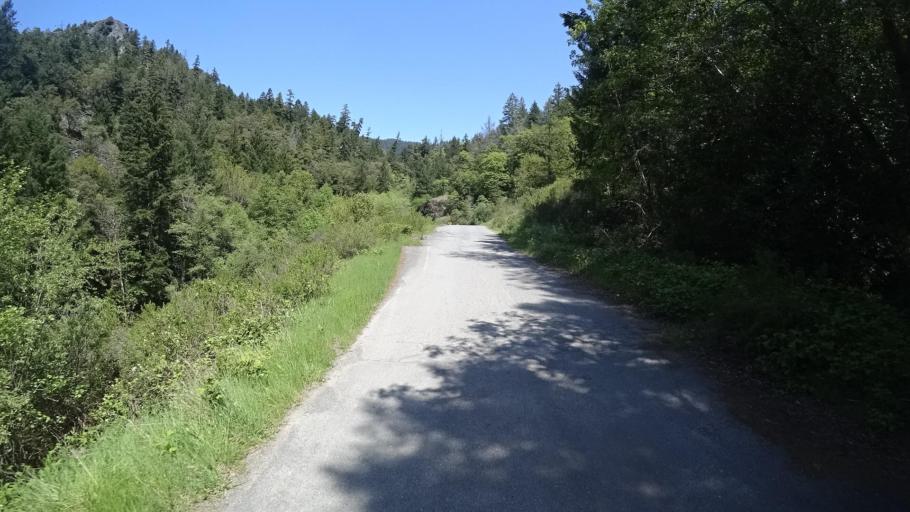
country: US
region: California
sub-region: Humboldt County
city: Redway
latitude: 40.2022
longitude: -123.5184
